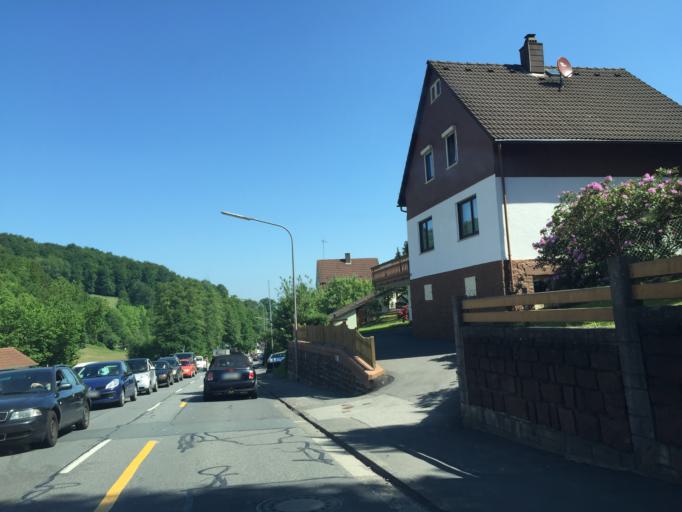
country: DE
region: Hesse
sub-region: Regierungsbezirk Darmstadt
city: Erbach
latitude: 49.6255
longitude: 8.9941
